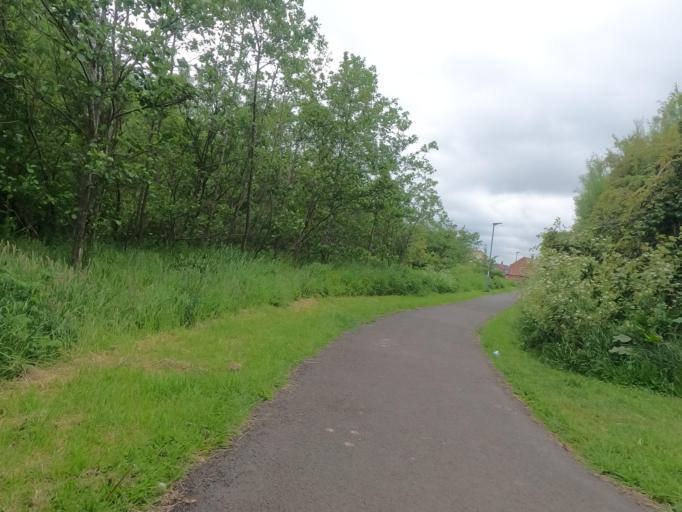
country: GB
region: England
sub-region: Northumberland
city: Blyth
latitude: 55.1205
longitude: -1.5373
